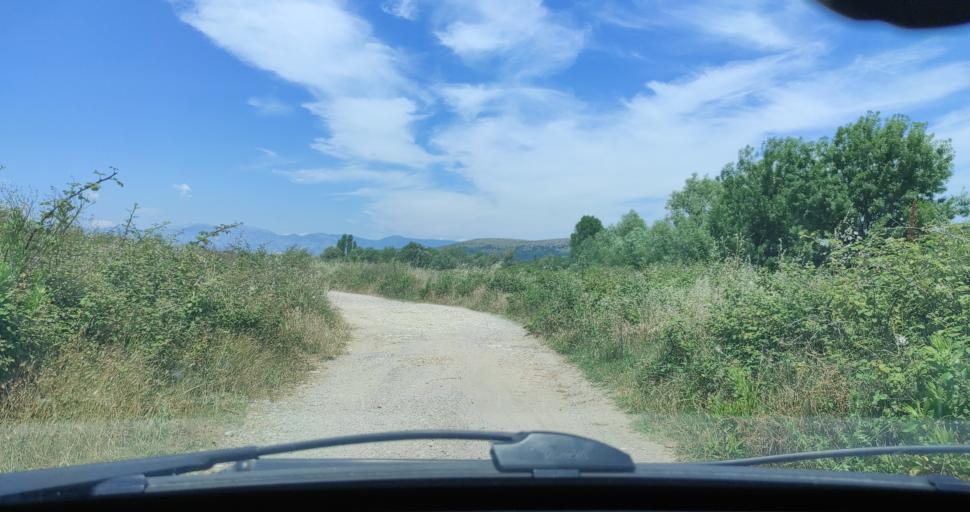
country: AL
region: Shkoder
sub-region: Rrethi i Shkodres
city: Velipoje
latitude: 41.8808
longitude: 19.3940
